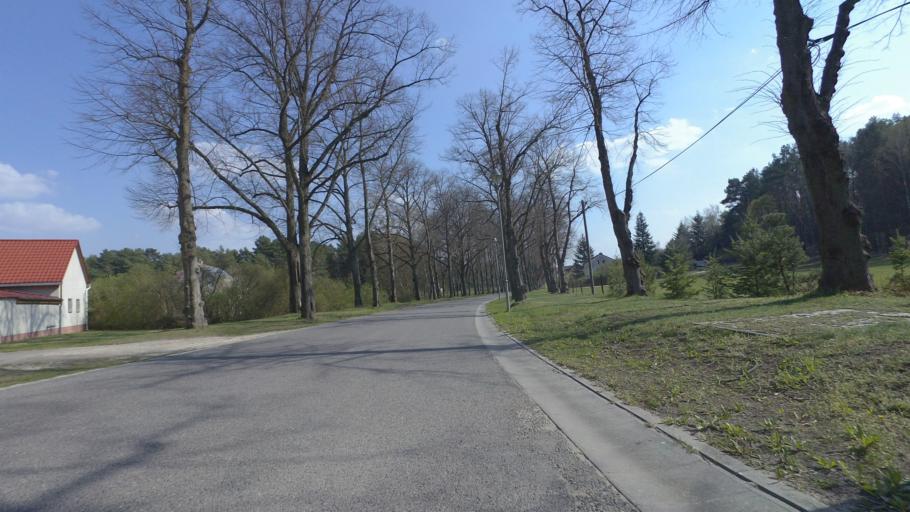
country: DE
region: Brandenburg
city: Teupitz
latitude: 52.1766
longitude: 13.5690
